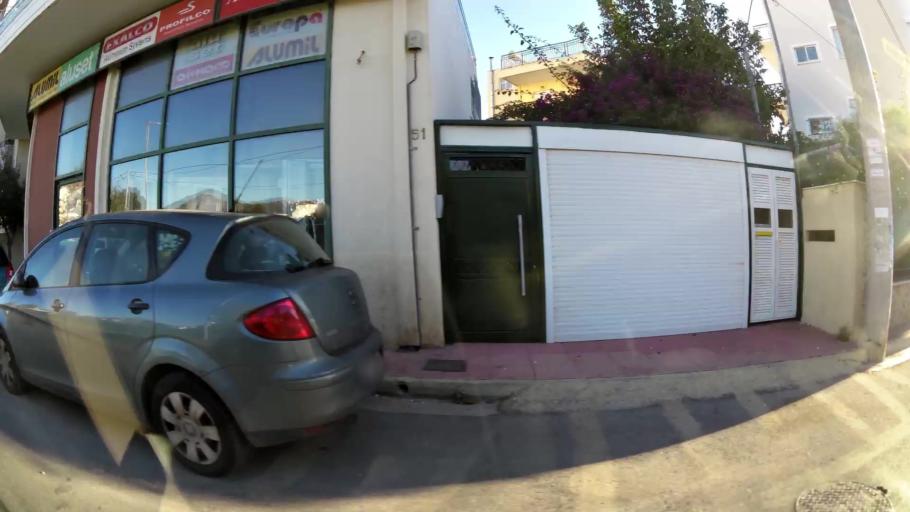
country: GR
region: Attica
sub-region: Nomarchia Anatolikis Attikis
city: Koropi
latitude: 37.9062
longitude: 23.8764
